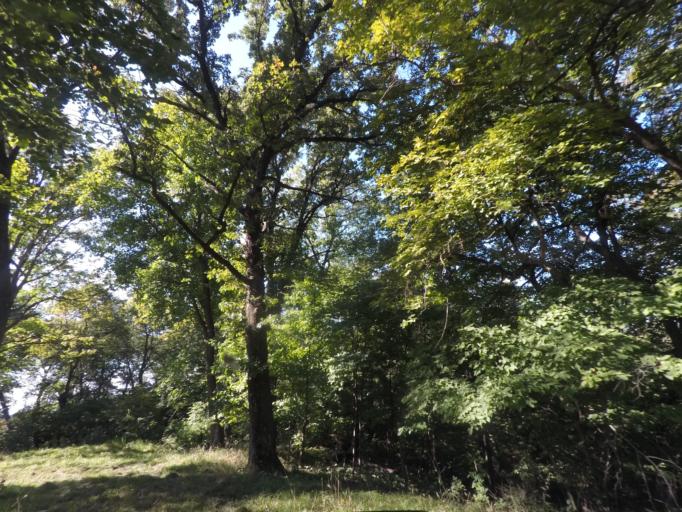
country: US
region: Iowa
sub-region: Story County
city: Nevada
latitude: 42.0336
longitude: -93.3739
